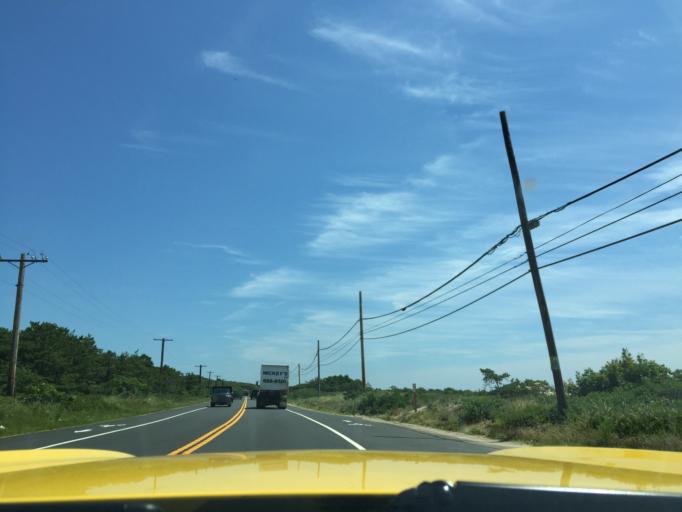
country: US
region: New York
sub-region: Suffolk County
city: Montauk
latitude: 41.0039
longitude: -72.0258
